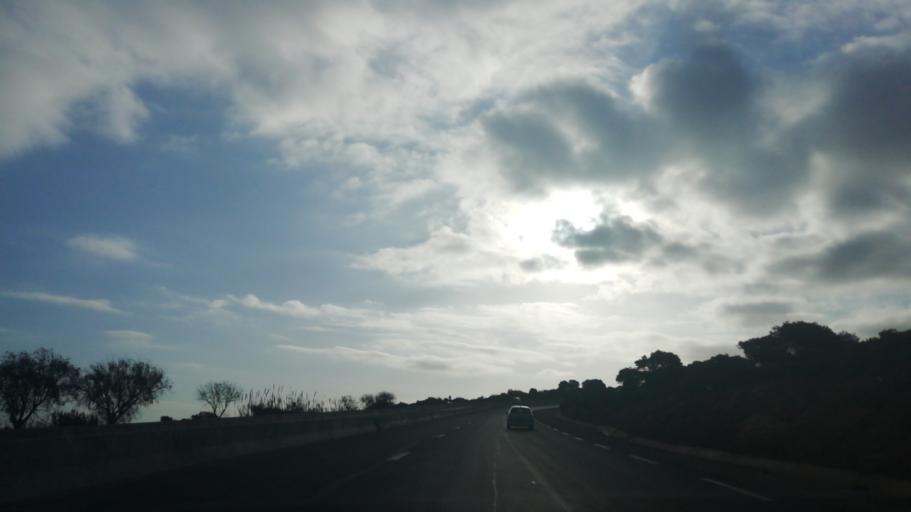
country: DZ
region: Mostaganem
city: Mostaganem
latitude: 36.1101
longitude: 0.2613
